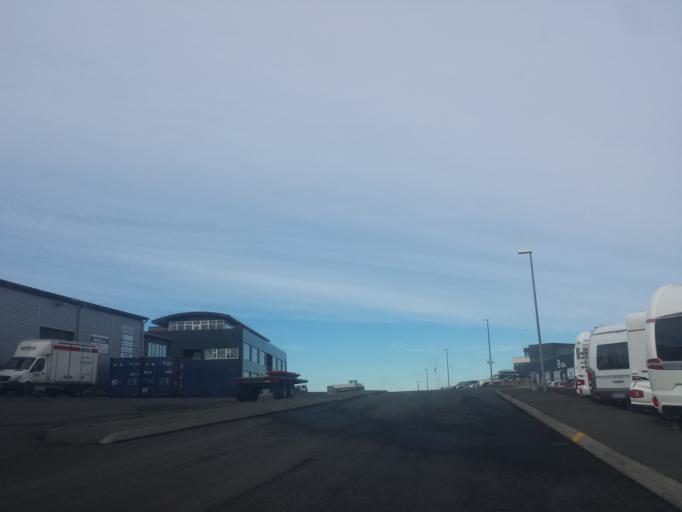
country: IS
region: Capital Region
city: Reykjavik
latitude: 64.0958
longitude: -21.8103
